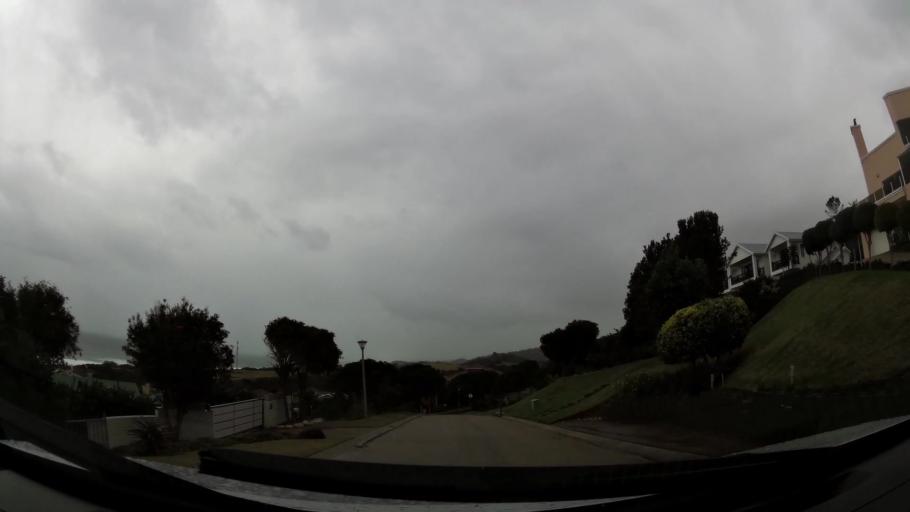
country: ZA
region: Western Cape
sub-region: Eden District Municipality
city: Mossel Bay
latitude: -34.0462
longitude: 22.2844
